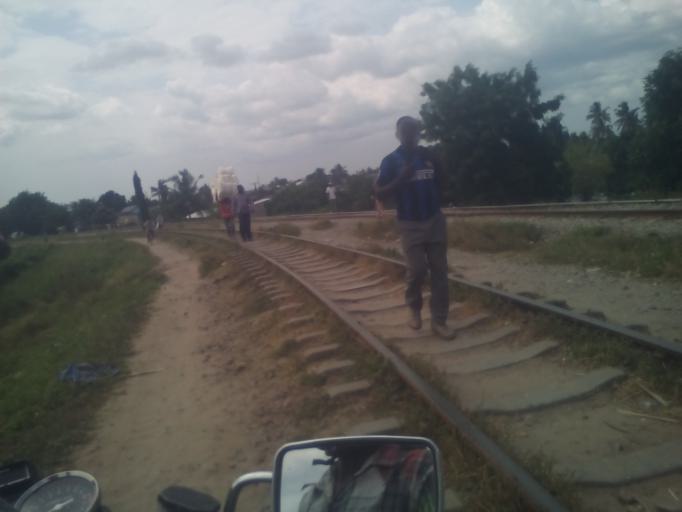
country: TZ
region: Dar es Salaam
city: Dar es Salaam
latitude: -6.8640
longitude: 39.2451
